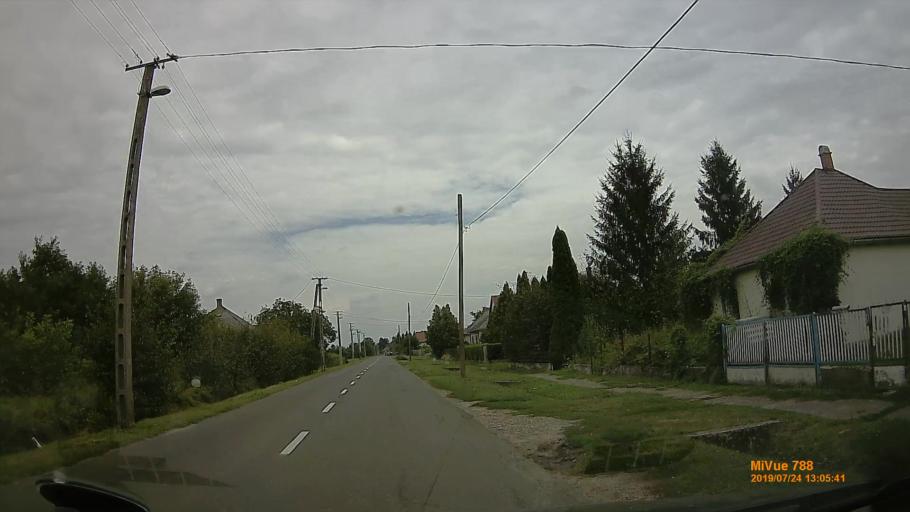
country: HU
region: Szabolcs-Szatmar-Bereg
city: Aranyosapati
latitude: 48.1946
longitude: 22.2964
